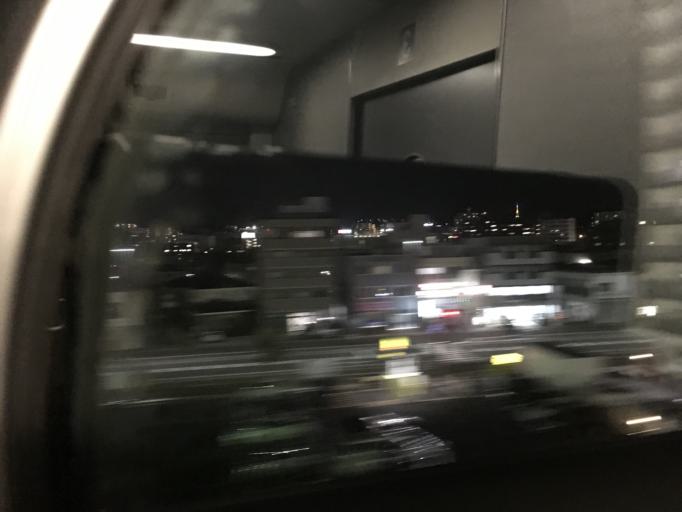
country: JP
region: Miyagi
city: Sendai
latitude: 38.2228
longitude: 140.8842
